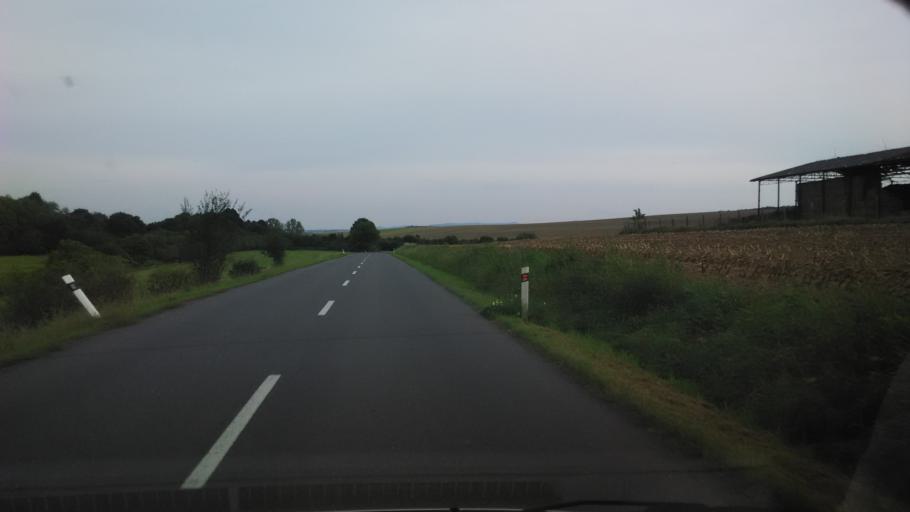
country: SK
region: Banskobystricky
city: Dudince
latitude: 48.2013
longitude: 18.8078
